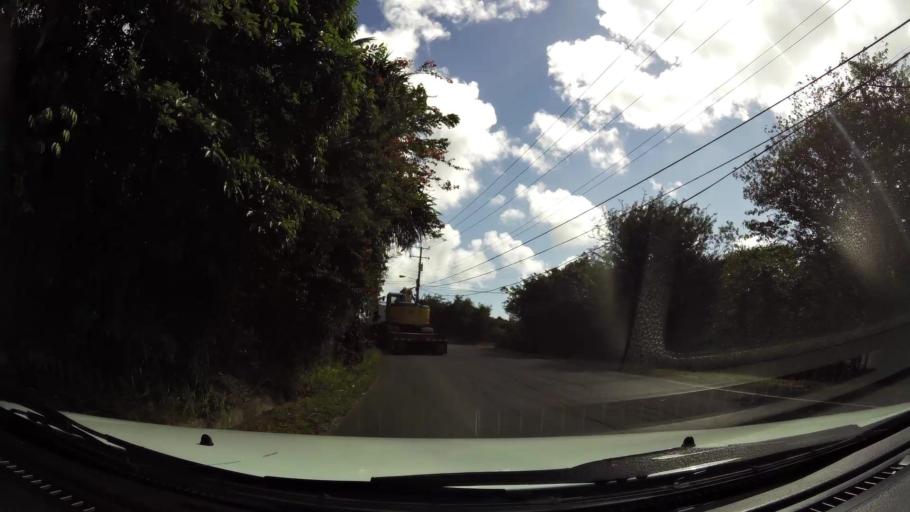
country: LC
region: Laborie Quarter
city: Laborie
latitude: 13.7524
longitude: -61.0065
